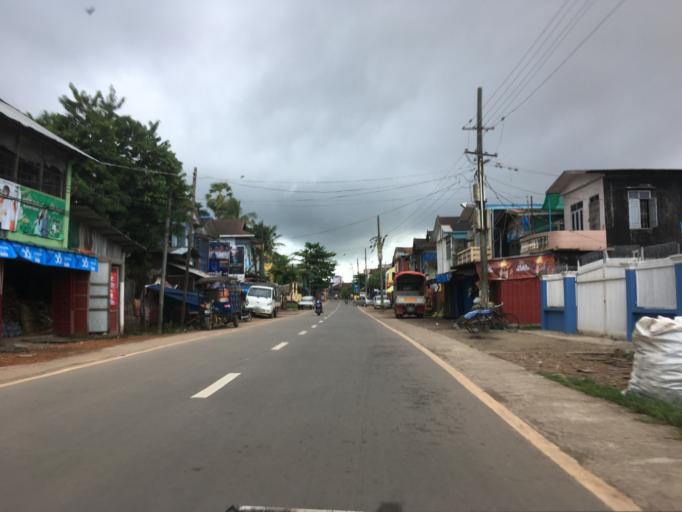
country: MM
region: Mon
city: Mawlamyine
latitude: 16.4642
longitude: 97.6241
